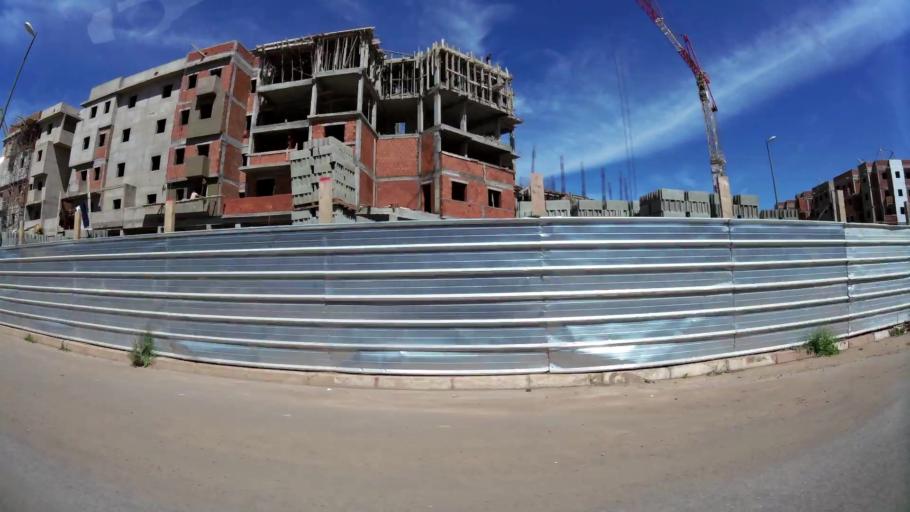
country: MA
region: Marrakech-Tensift-Al Haouz
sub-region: Marrakech
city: Marrakesh
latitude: 31.6341
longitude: -8.0743
